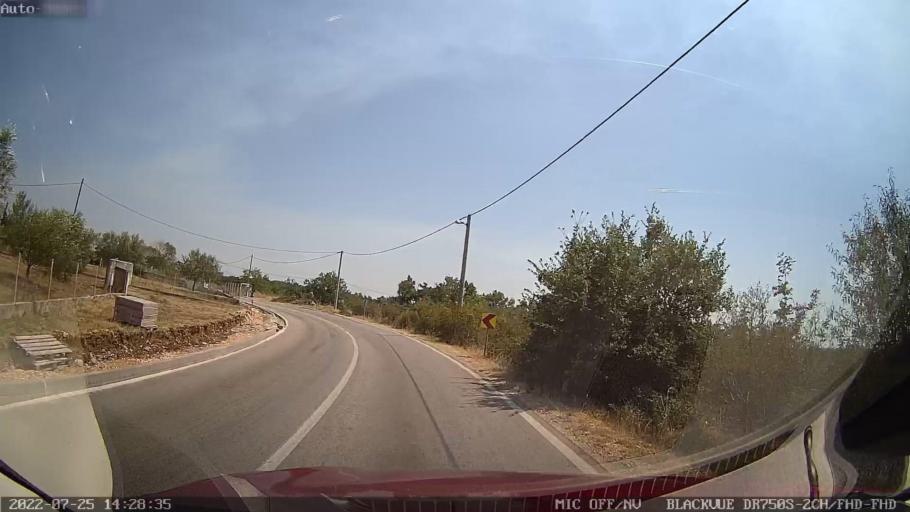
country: HR
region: Zadarska
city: Policnik
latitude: 44.1250
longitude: 15.3492
